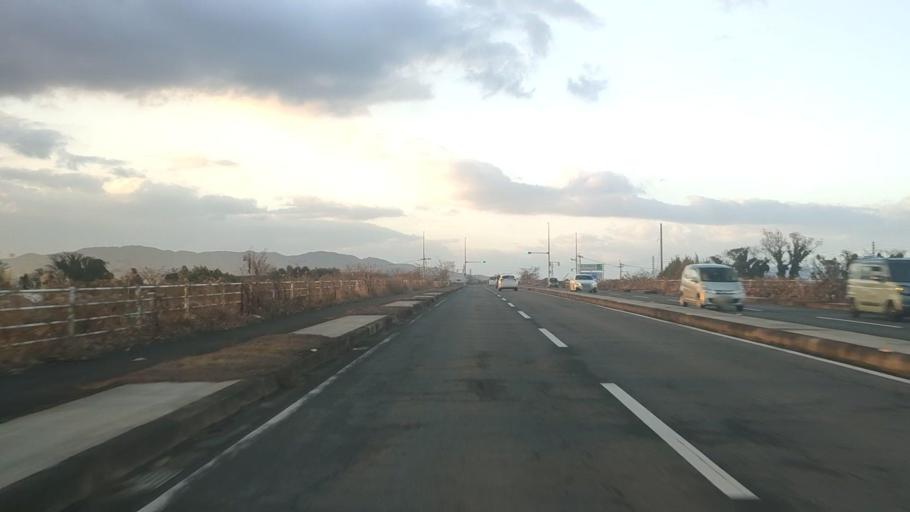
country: JP
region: Kumamoto
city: Kumamoto
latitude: 32.7440
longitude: 130.7056
